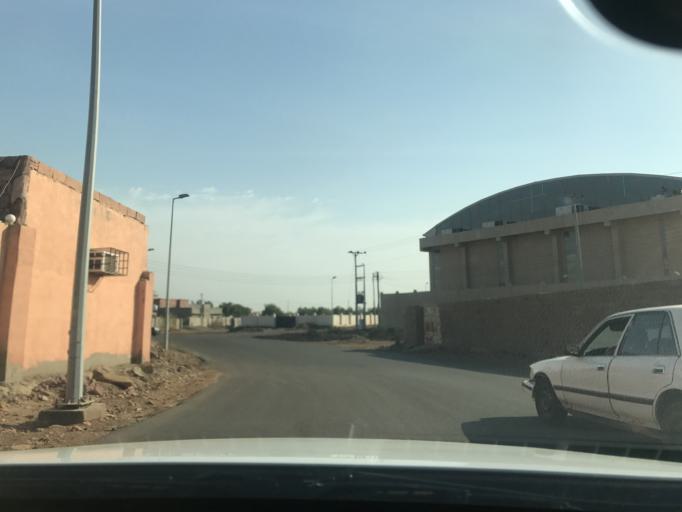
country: SA
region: Makkah
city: Al Jumum
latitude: 21.4498
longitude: 39.5382
